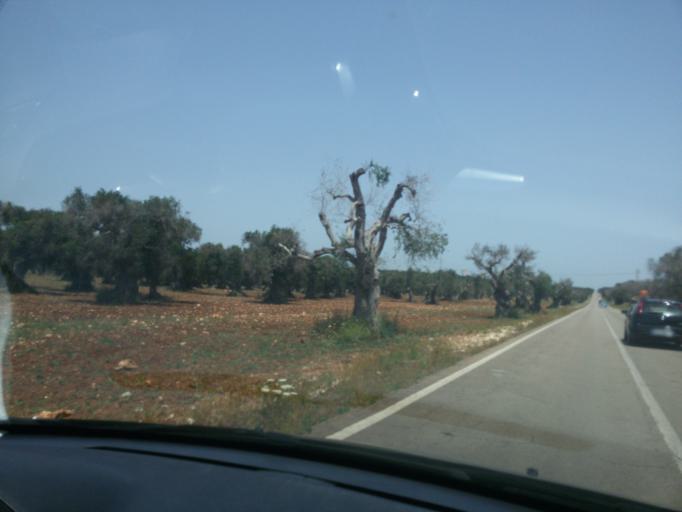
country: IT
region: Apulia
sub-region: Provincia di Lecce
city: Porto Cesareo
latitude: 40.2864
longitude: 17.9104
